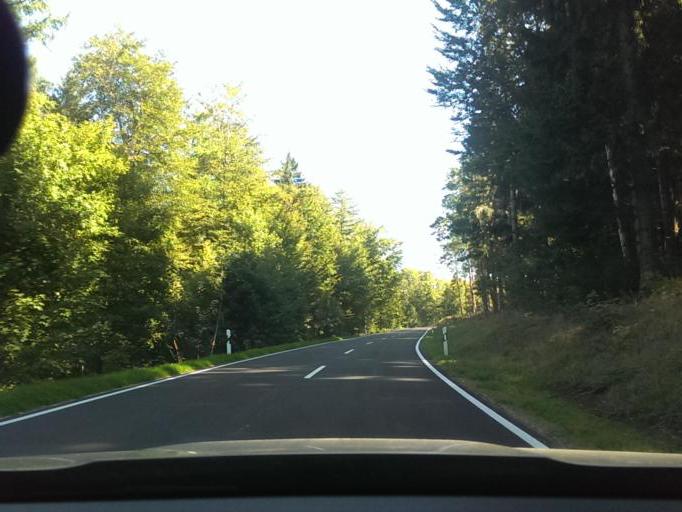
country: DE
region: Baden-Wuerttemberg
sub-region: Karlsruhe Region
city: Dobel
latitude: 48.8046
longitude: 8.4723
